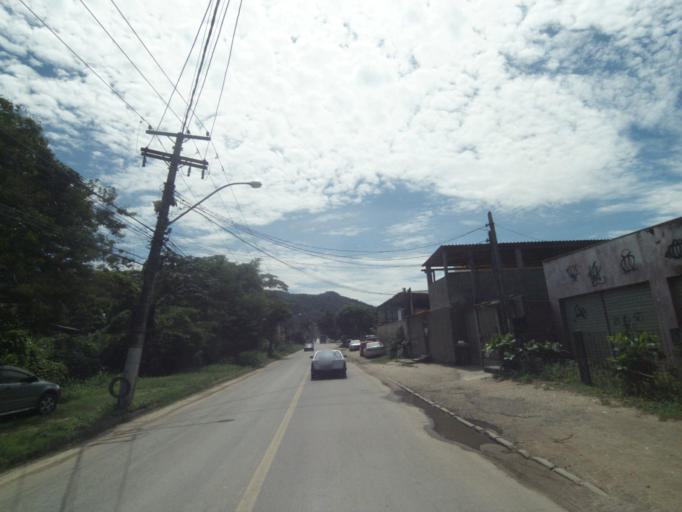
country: BR
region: Rio de Janeiro
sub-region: Niteroi
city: Niteroi
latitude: -22.9293
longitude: -43.0080
